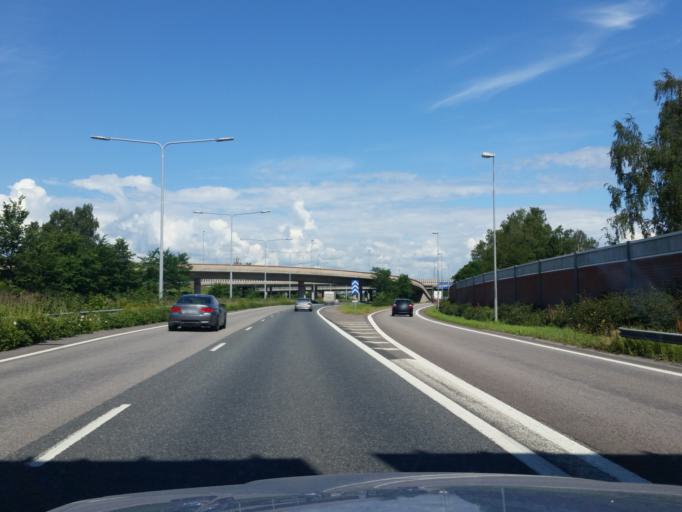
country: FI
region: Uusimaa
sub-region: Helsinki
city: Helsinki
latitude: 60.2414
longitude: 24.9480
